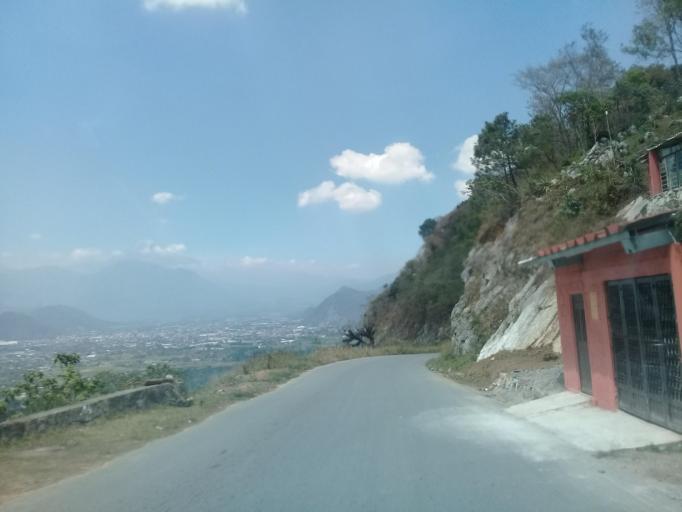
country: MX
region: Veracruz
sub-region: Tlilapan
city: Tonalixco
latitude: 18.8020
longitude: -97.0587
